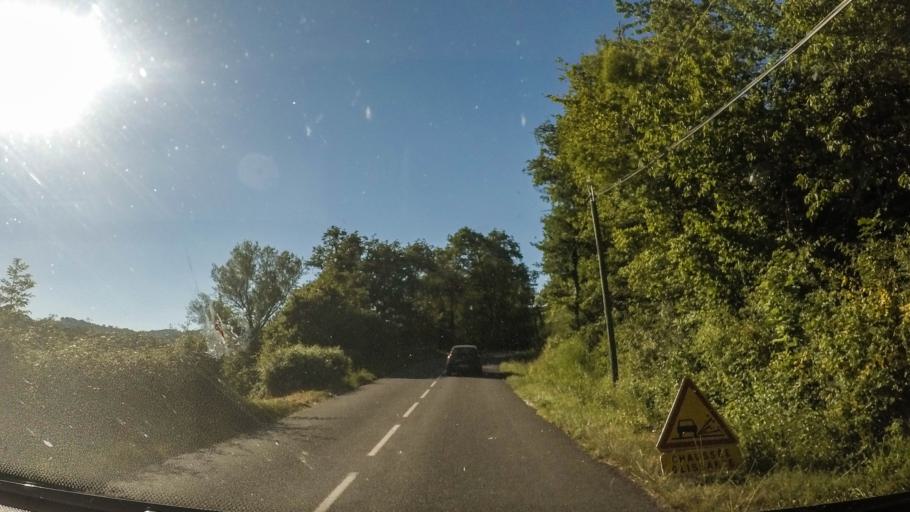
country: FR
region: Midi-Pyrenees
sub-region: Departement de l'Aveyron
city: Saint-Christophe-Vallon
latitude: 44.5516
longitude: 2.3970
